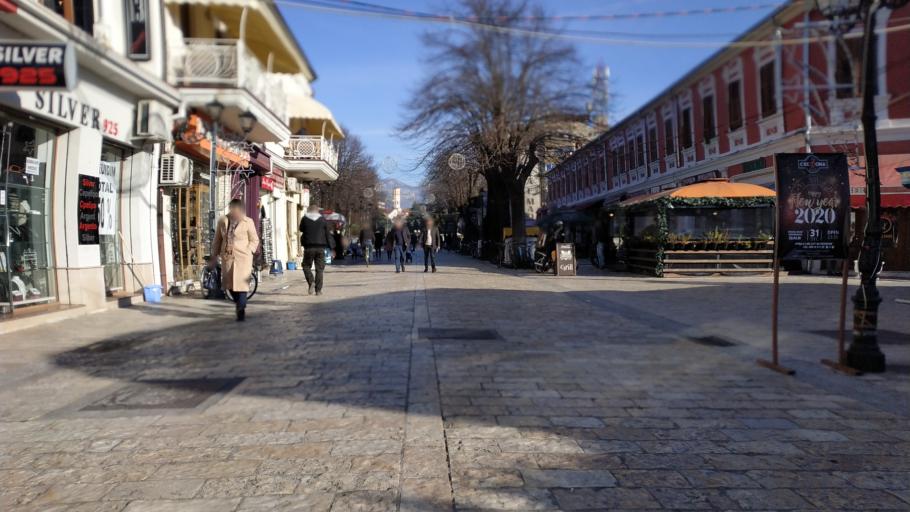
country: AL
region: Shkoder
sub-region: Rrethi i Shkodres
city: Shkoder
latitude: 42.0658
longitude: 19.5129
